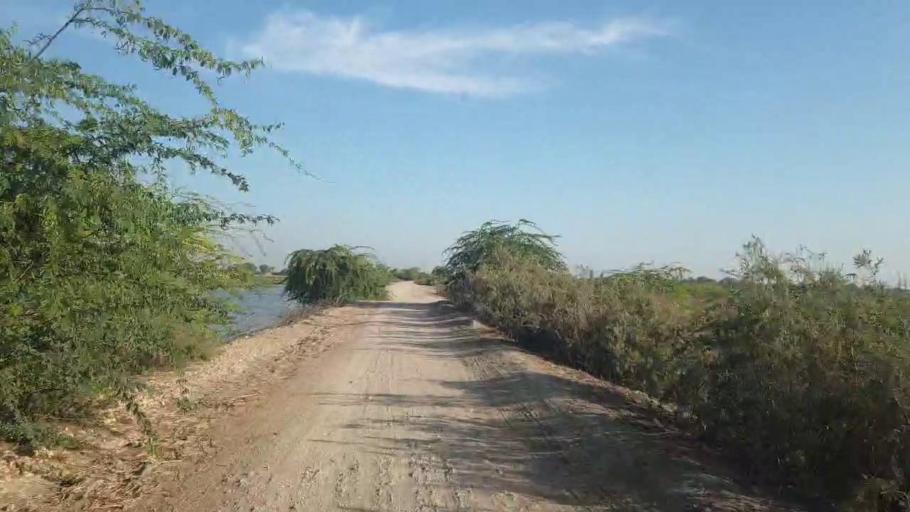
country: PK
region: Sindh
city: Talhar
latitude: 24.8196
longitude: 68.8384
